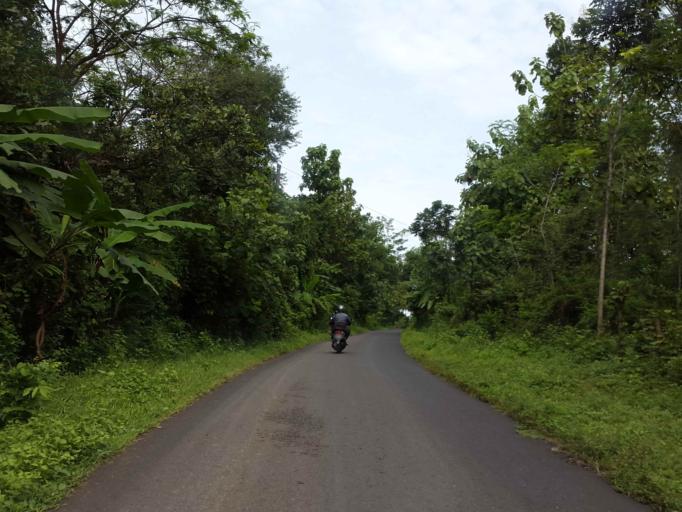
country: ID
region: Central Java
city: Randudongkal
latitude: -7.0488
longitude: 109.3497
